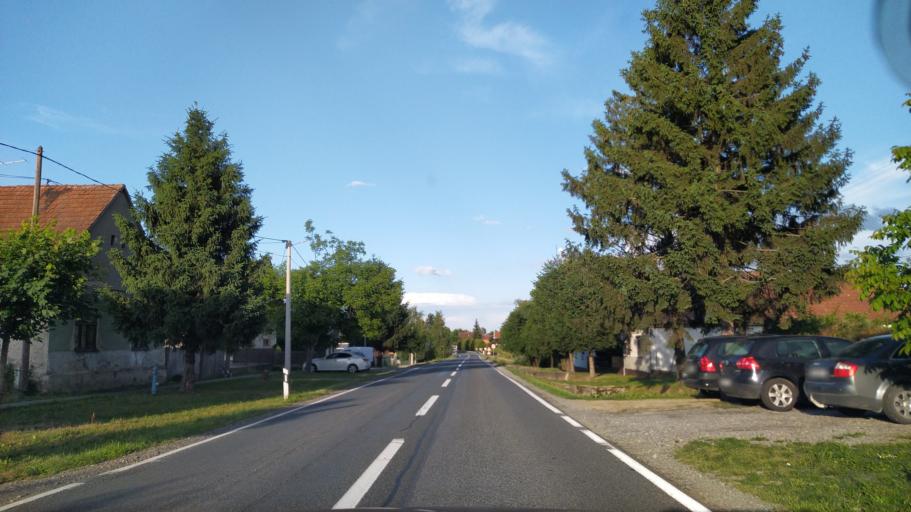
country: HR
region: Virovitick-Podravska
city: Cacinci
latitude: 45.5997
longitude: 17.8579
